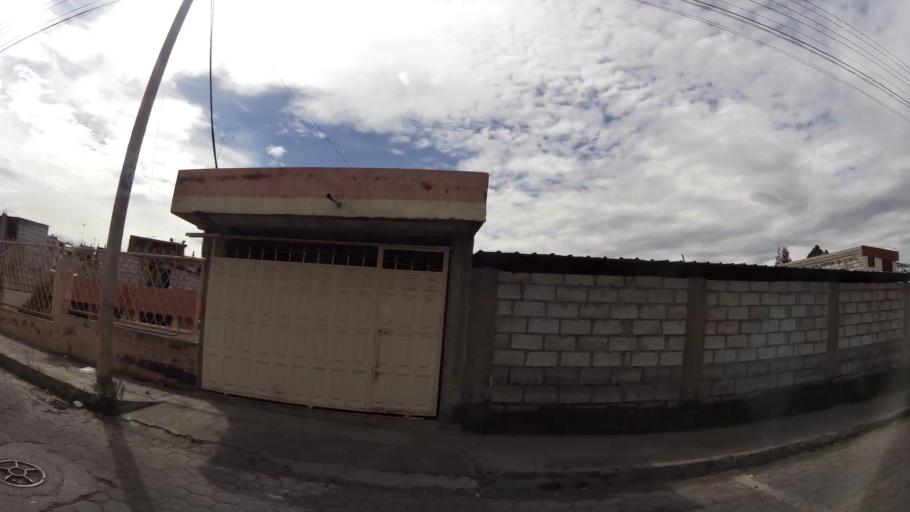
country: EC
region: Cotopaxi
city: Latacunga
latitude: -0.9276
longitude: -78.6043
